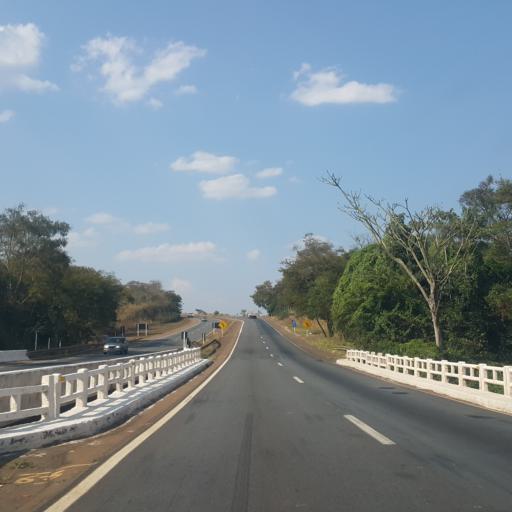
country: BR
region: Goias
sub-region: Abadiania
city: Abadiania
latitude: -16.2973
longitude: -48.8050
